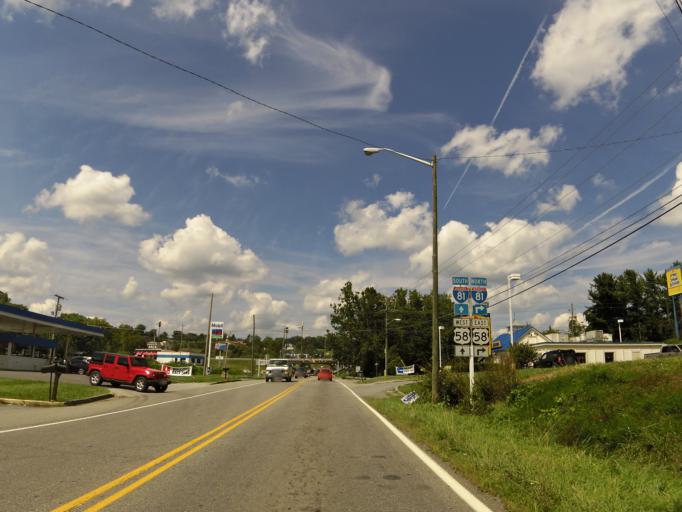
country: US
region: Virginia
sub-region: Washington County
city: Abingdon
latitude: 36.6977
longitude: -81.9741
